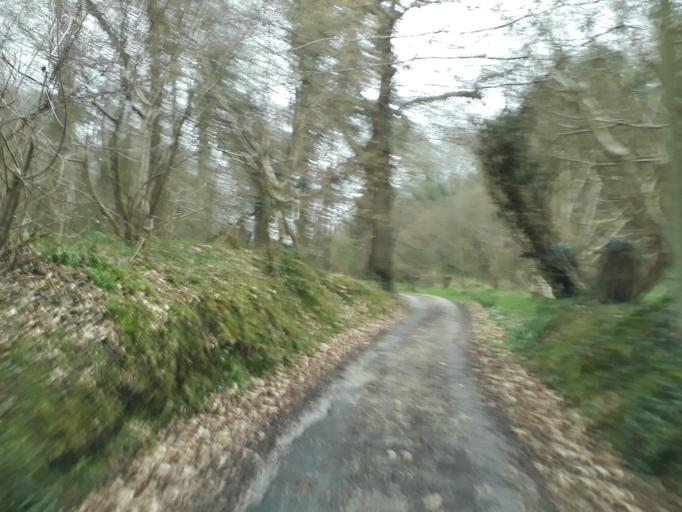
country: FR
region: Haute-Normandie
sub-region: Departement de la Seine-Maritime
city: Yport
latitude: 49.7288
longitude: 0.2962
